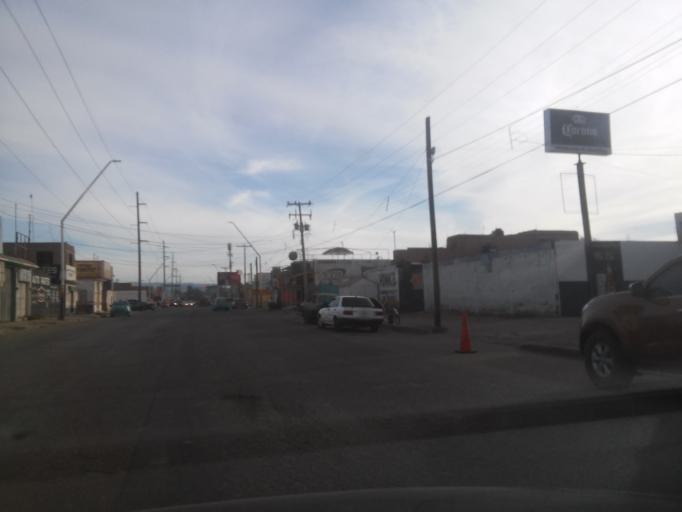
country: MX
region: Durango
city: Victoria de Durango
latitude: 24.0151
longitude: -104.6326
